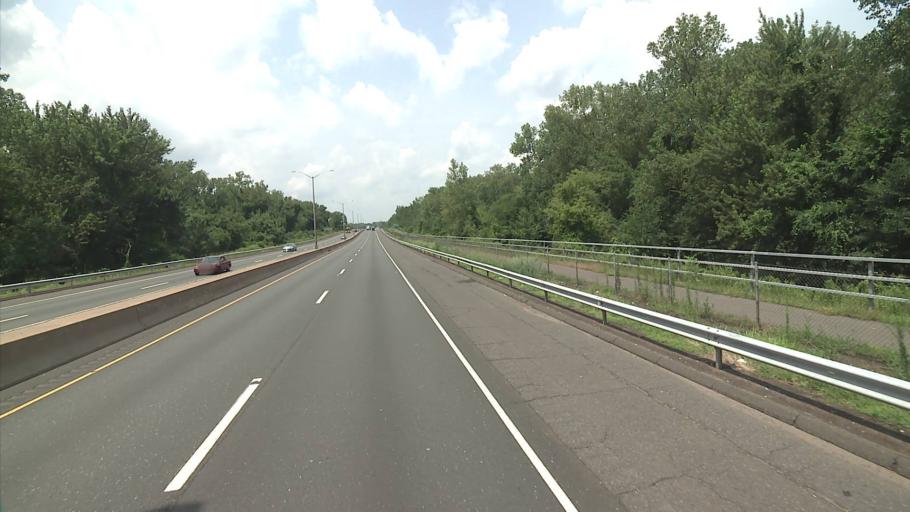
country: US
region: Connecticut
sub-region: Hartford County
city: South Windsor
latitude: 41.8112
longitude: -72.6369
